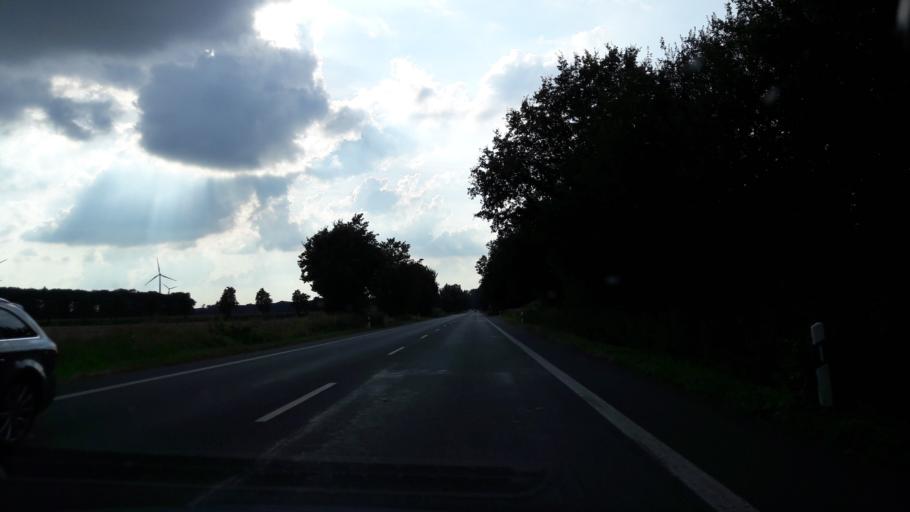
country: DE
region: North Rhine-Westphalia
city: Ahlen
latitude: 51.8218
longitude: 7.9065
